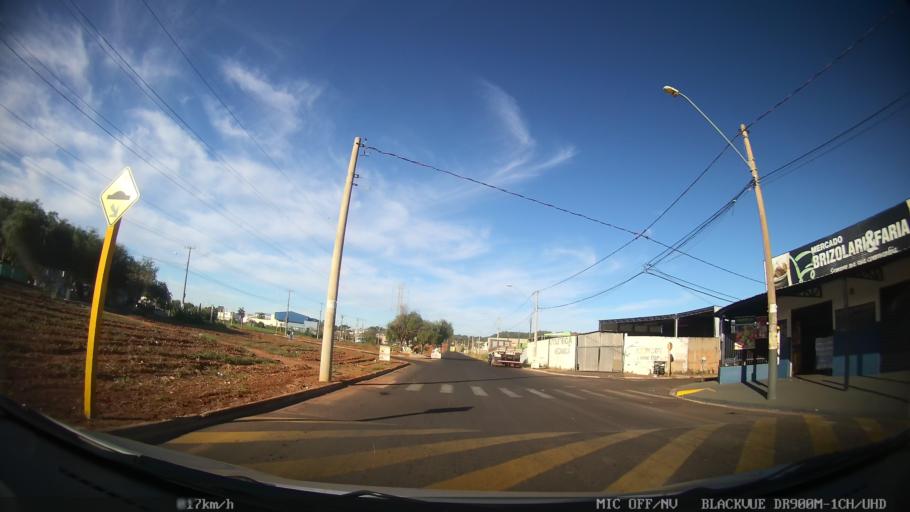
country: BR
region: Sao Paulo
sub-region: Americo Brasiliense
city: Americo Brasiliense
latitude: -21.7475
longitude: -48.1409
